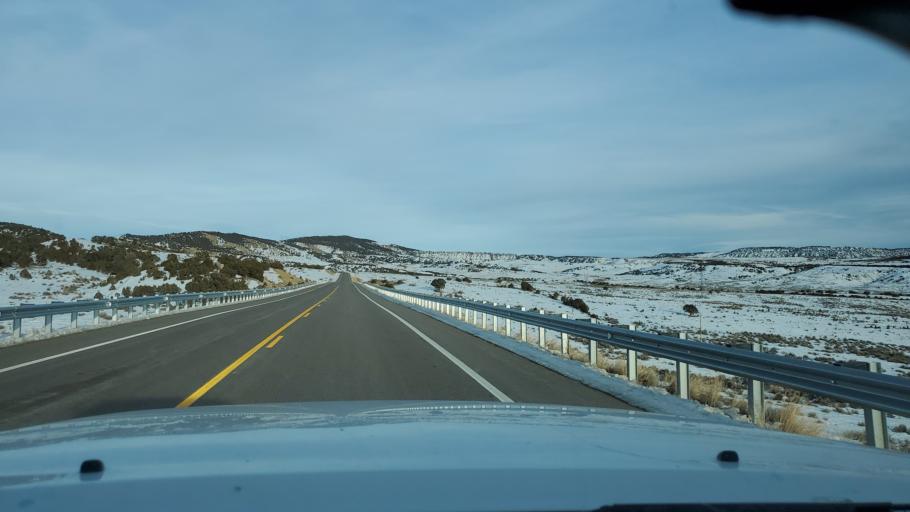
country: US
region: Colorado
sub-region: Rio Blanco County
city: Rangely
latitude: 40.3388
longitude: -108.4713
